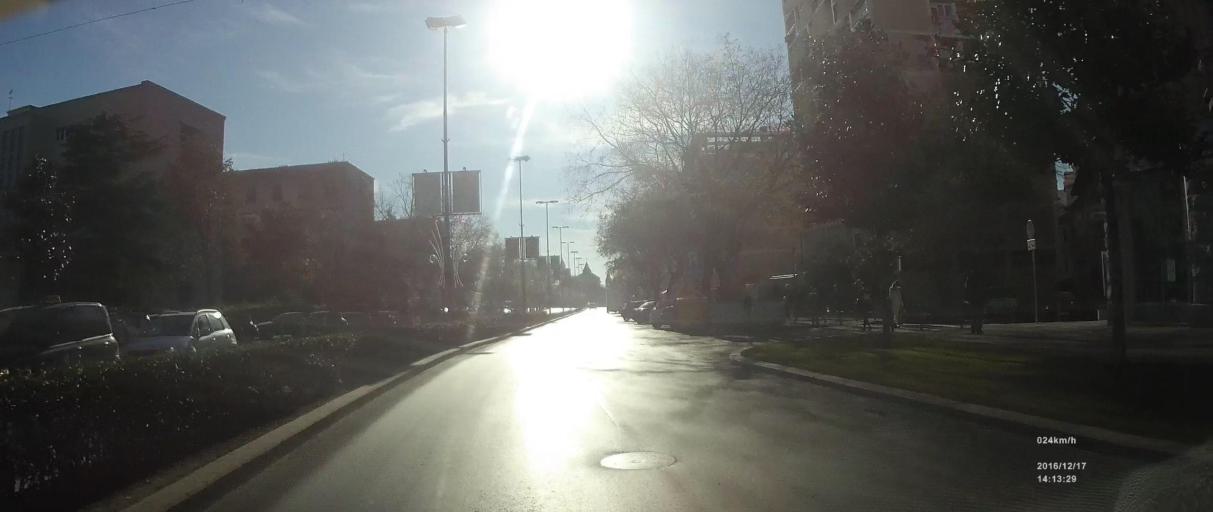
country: HR
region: Splitsko-Dalmatinska
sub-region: Grad Split
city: Split
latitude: 43.5144
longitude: 16.4435
